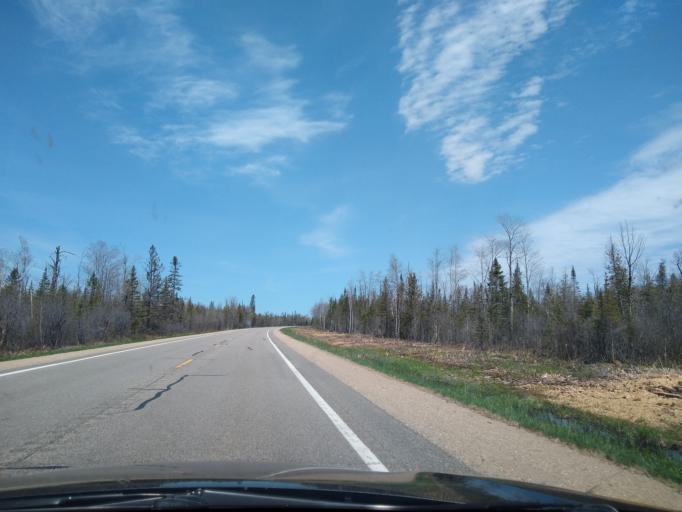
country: US
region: Michigan
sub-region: Delta County
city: Gladstone
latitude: 46.0339
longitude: -86.9808
